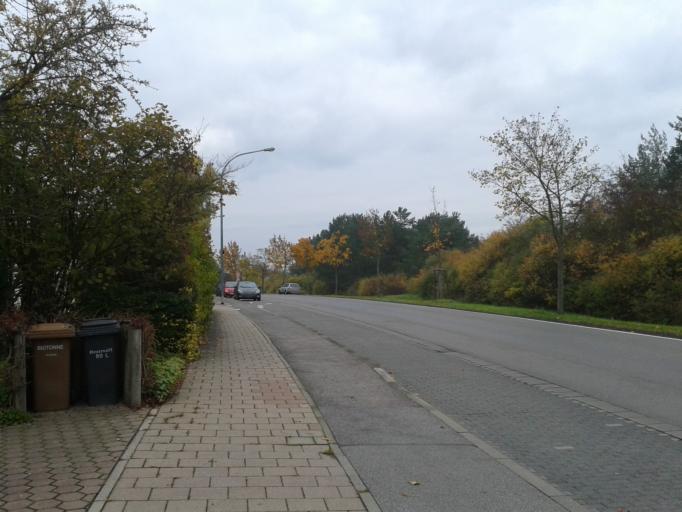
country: DE
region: Bavaria
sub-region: Upper Franconia
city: Gundelsheim
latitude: 49.9224
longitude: 10.9111
